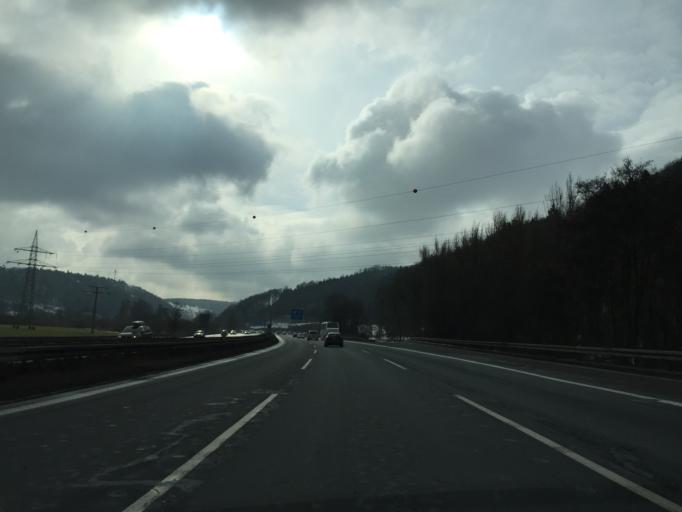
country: DE
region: Bavaria
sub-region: Regierungsbezirk Mittelfranken
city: Greding
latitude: 49.0086
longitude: 11.3543
